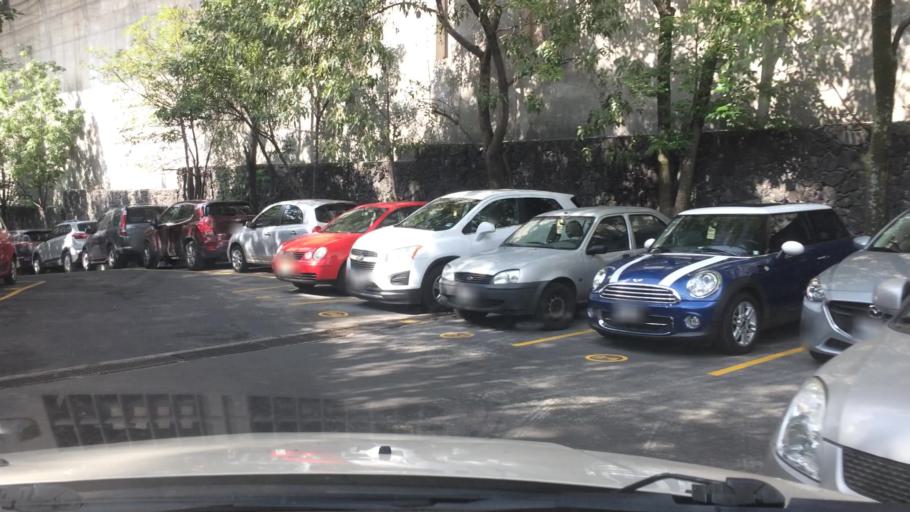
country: MX
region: Mexico City
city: Tlalpan
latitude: 19.3041
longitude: -99.1769
